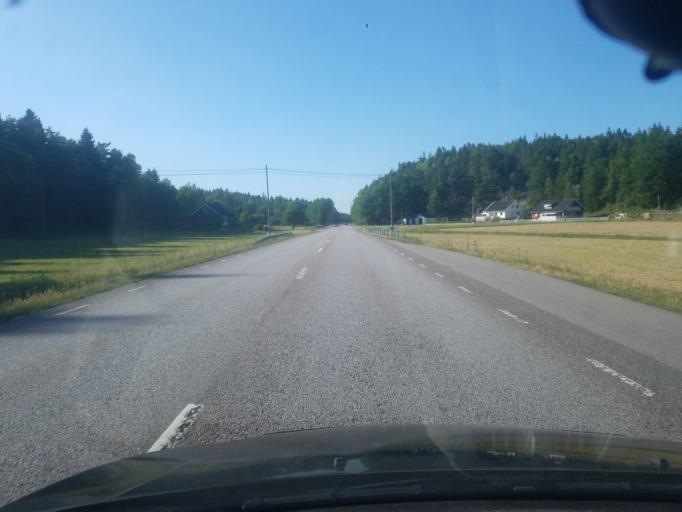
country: SE
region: Vaestra Goetaland
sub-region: Orust
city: Henan
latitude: 58.1815
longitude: 11.6950
